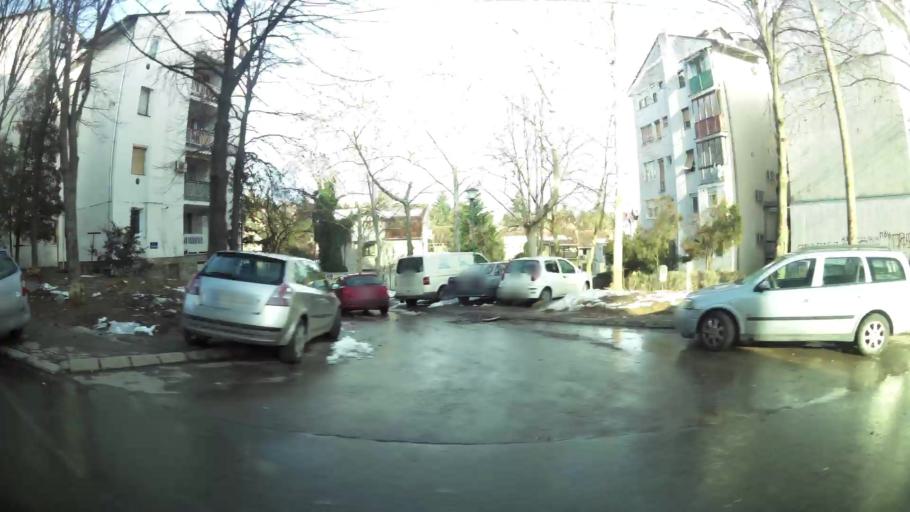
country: RS
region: Central Serbia
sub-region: Belgrade
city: Rakovica
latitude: 44.7228
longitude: 20.4221
